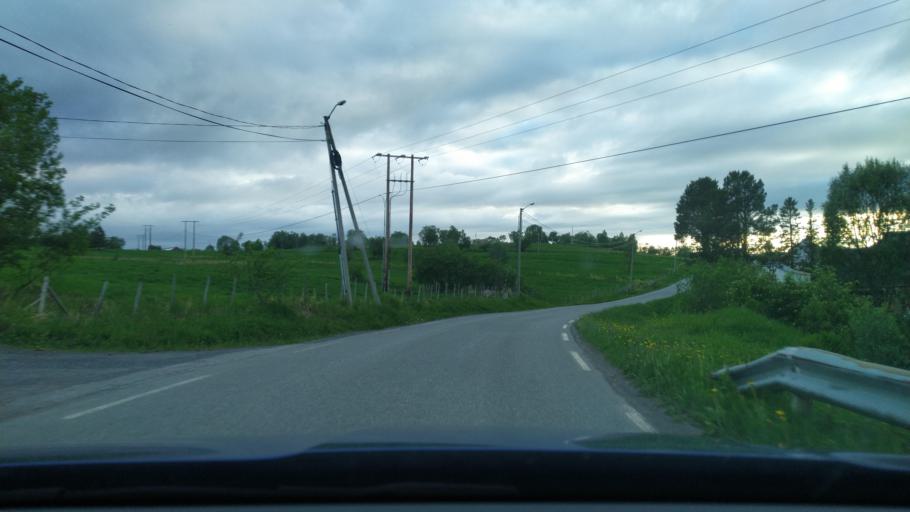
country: NO
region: Troms
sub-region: Tranoy
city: Vangsvika
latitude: 69.1261
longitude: 17.8543
